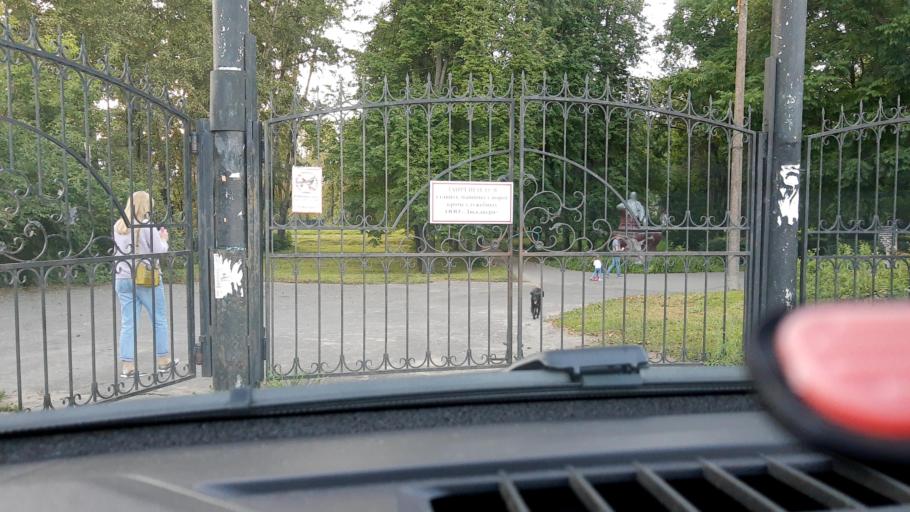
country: RU
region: Nizjnij Novgorod
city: Bor
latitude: 56.3643
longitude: 44.0510
